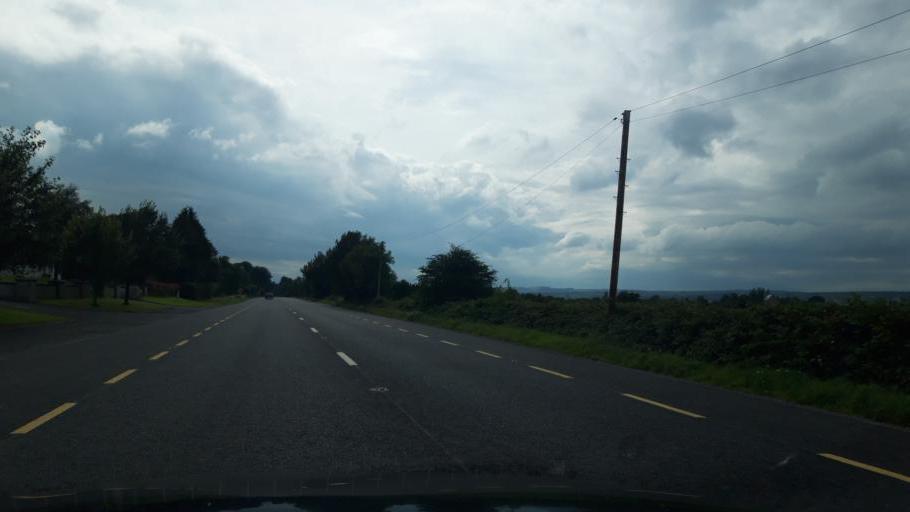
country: IE
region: Leinster
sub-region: Kilkenny
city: Castlecomer
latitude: 52.8393
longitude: -7.1425
